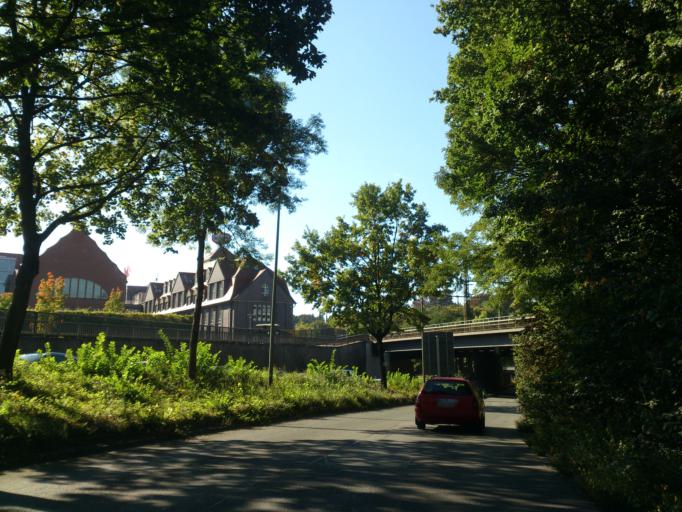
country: DE
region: North Rhine-Westphalia
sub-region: Regierungsbezirk Detmold
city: Bielefeld
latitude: 52.0166
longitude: 8.5224
